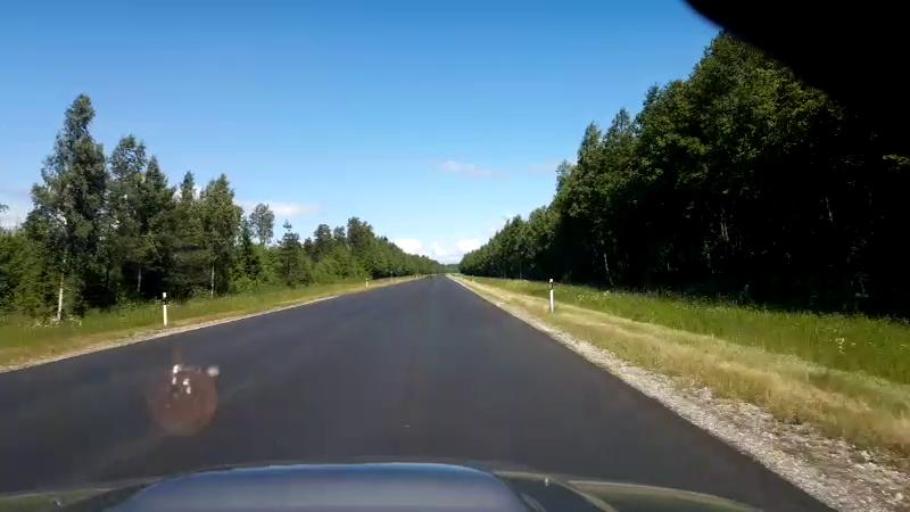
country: LV
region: Salacgrivas
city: Ainazi
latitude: 57.9292
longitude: 24.4260
